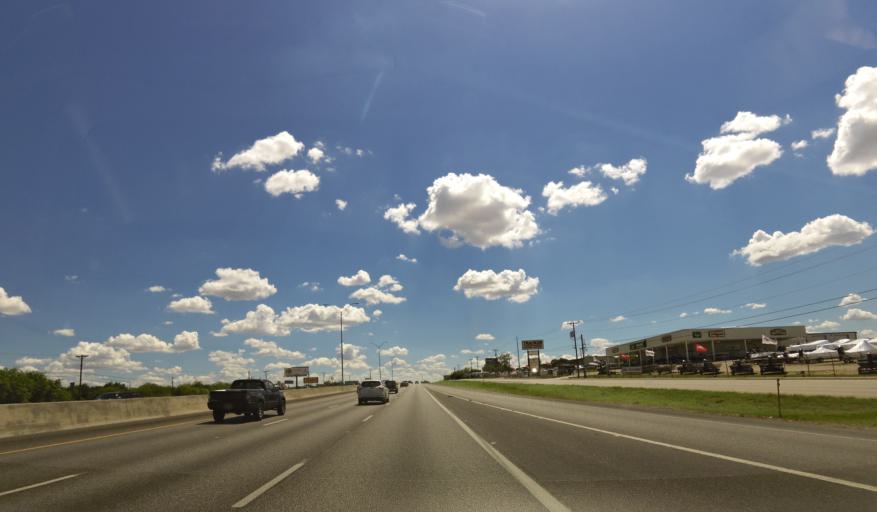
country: US
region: Texas
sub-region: Guadalupe County
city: Northcliff
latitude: 29.6503
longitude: -98.1948
